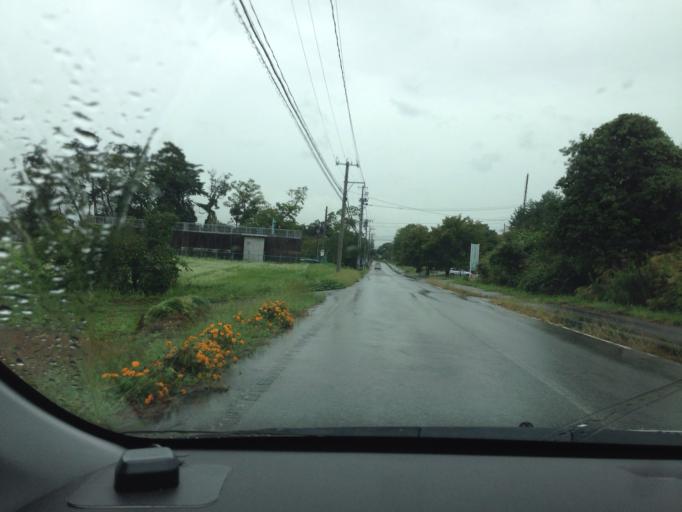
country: JP
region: Fukushima
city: Kitakata
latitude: 37.5077
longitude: 139.8113
